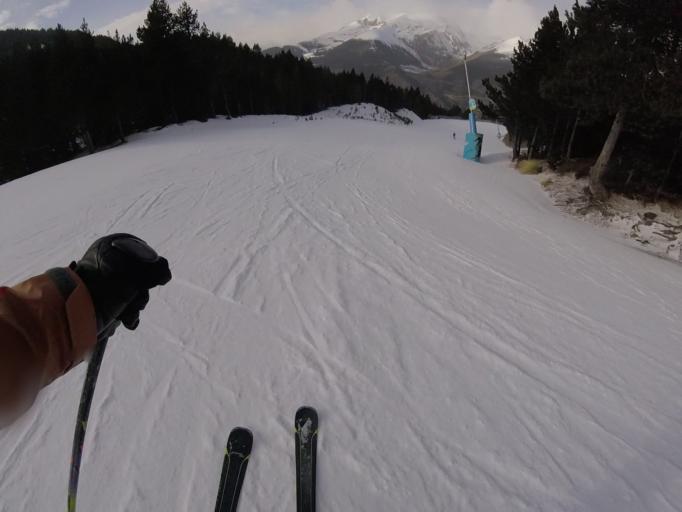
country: AD
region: Canillo
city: Canillo
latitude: 42.5502
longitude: 1.6141
